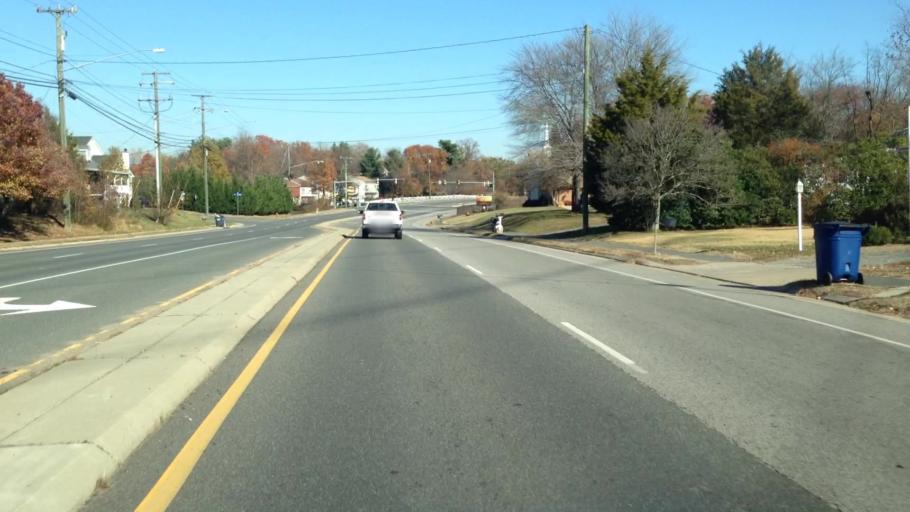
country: US
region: Virginia
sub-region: Fairfax County
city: Newington
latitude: 38.7559
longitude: -77.1638
